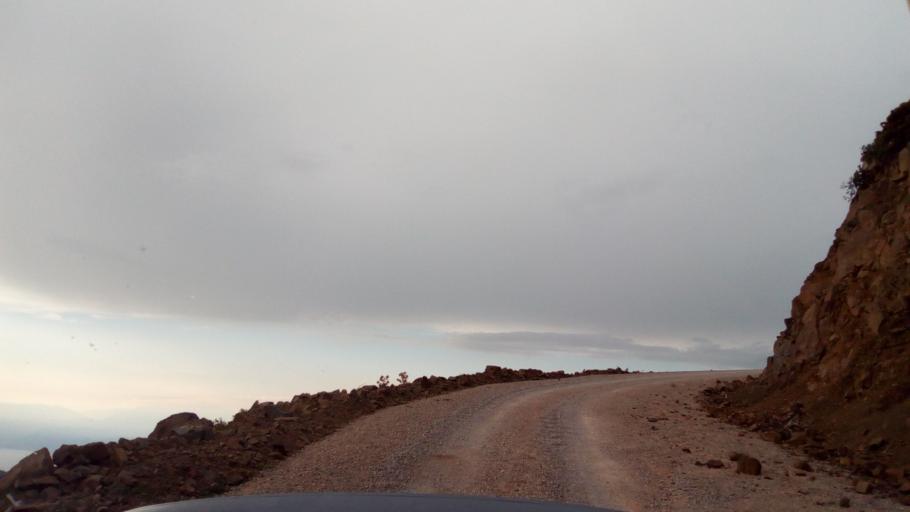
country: GR
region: Central Greece
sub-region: Nomos Fokidos
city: Lidoriki
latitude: 38.4556
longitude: 22.0789
